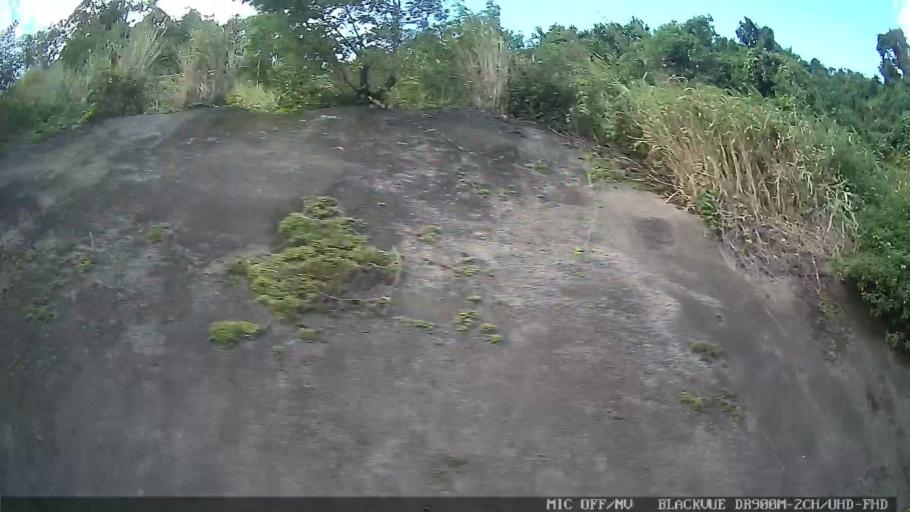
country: BR
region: Sao Paulo
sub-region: Guaruja
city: Guaruja
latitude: -23.9904
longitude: -46.2617
